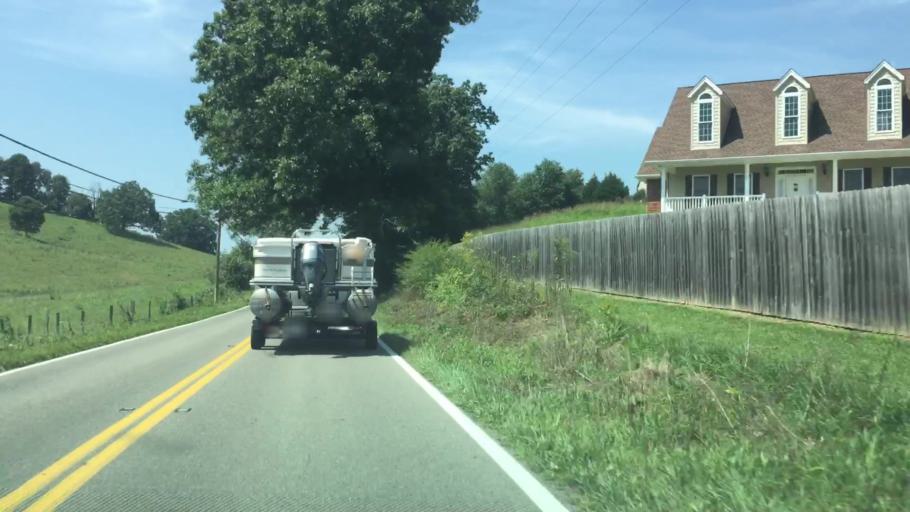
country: US
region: Virginia
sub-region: Washington County
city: Abingdon
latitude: 36.6546
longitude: -81.9778
